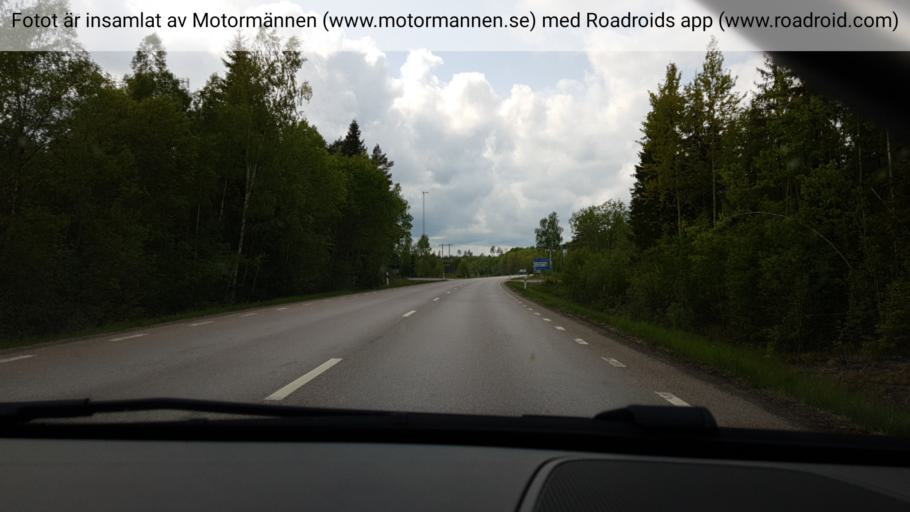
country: SE
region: Uppsala
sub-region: Tierps Kommun
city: Orbyhus
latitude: 60.2160
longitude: 17.7055
